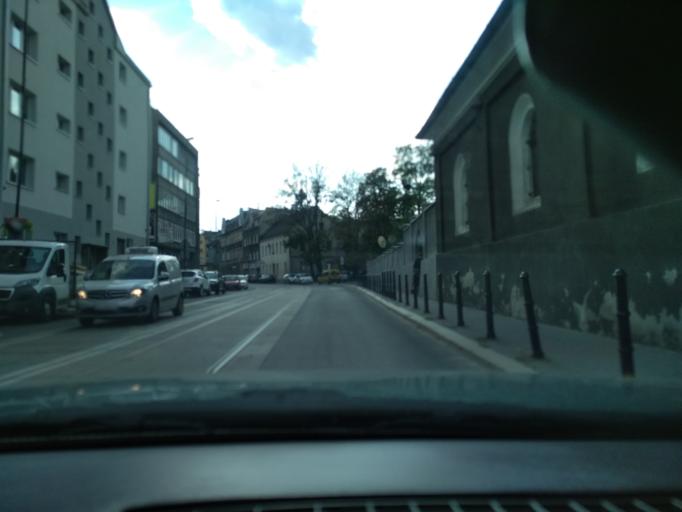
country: PL
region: Silesian Voivodeship
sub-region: Gliwice
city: Gliwice
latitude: 50.2964
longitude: 18.6573
